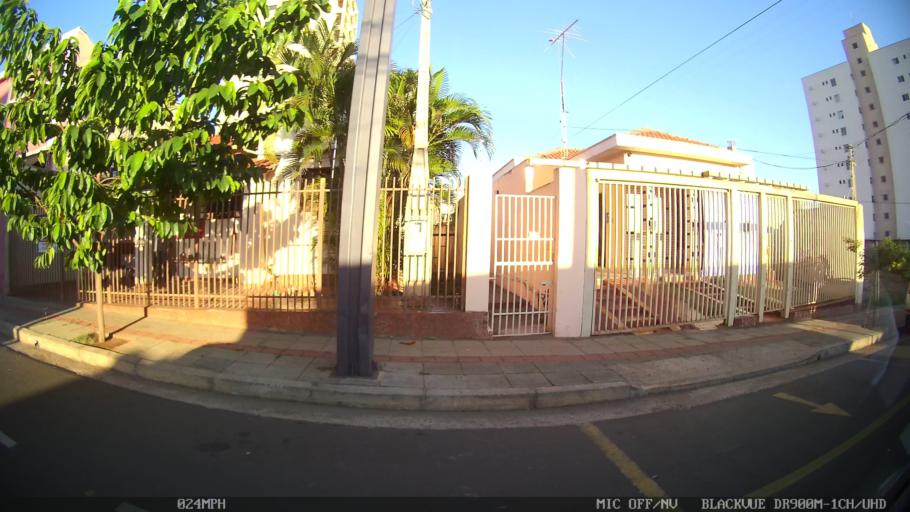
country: BR
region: Sao Paulo
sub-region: Sao Jose Do Rio Preto
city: Sao Jose do Rio Preto
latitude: -20.8035
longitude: -49.3736
